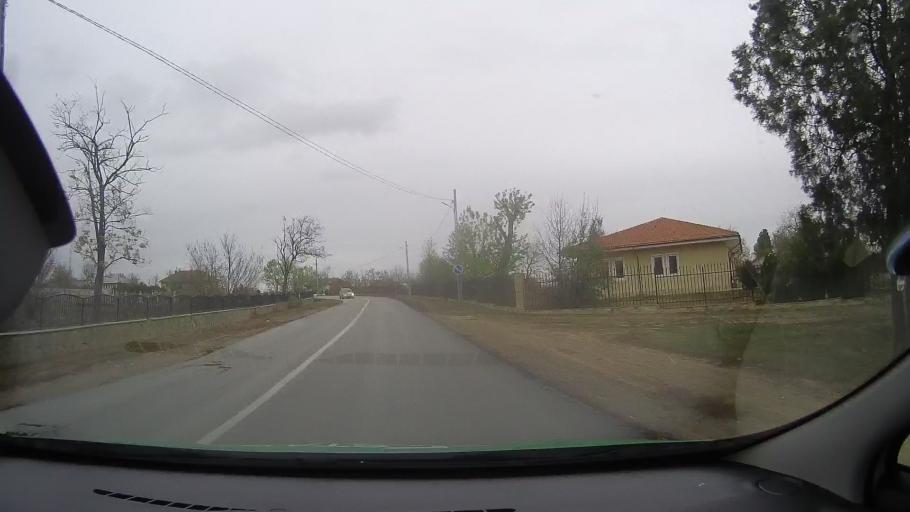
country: RO
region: Constanta
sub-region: Comuna Pantelimon
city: Pantelimon
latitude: 44.5475
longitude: 28.3290
